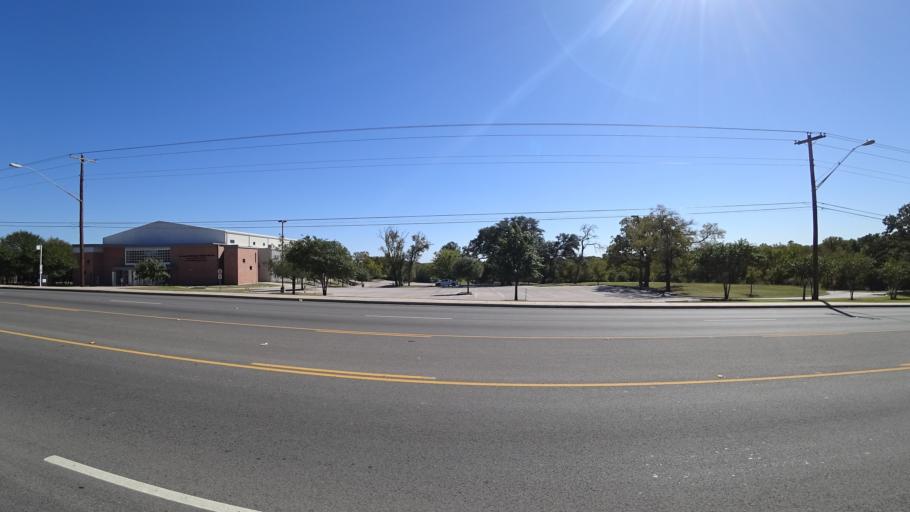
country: US
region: Texas
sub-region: Travis County
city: Austin
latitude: 30.2835
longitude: -97.6986
